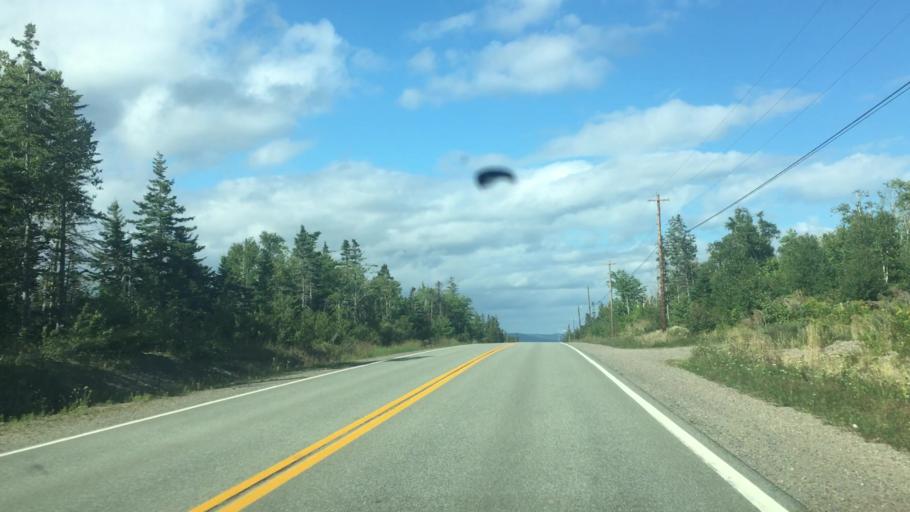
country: CA
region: Nova Scotia
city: Sydney
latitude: 45.8561
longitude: -60.6296
